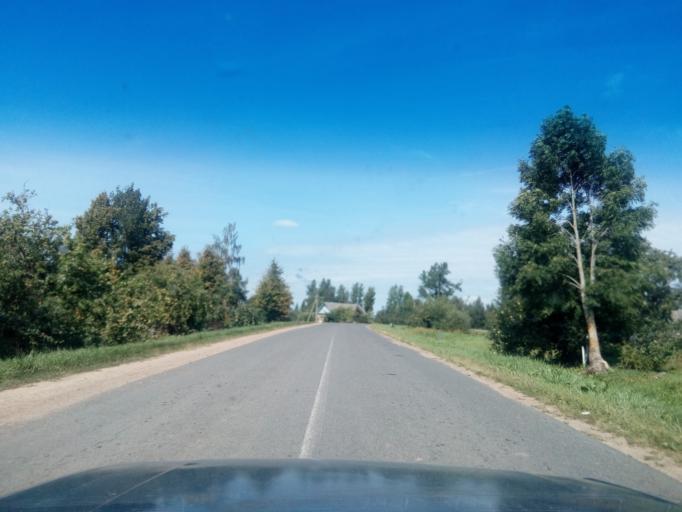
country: BY
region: Vitebsk
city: Vyerkhnyadzvinsk
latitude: 55.8317
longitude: 27.7354
